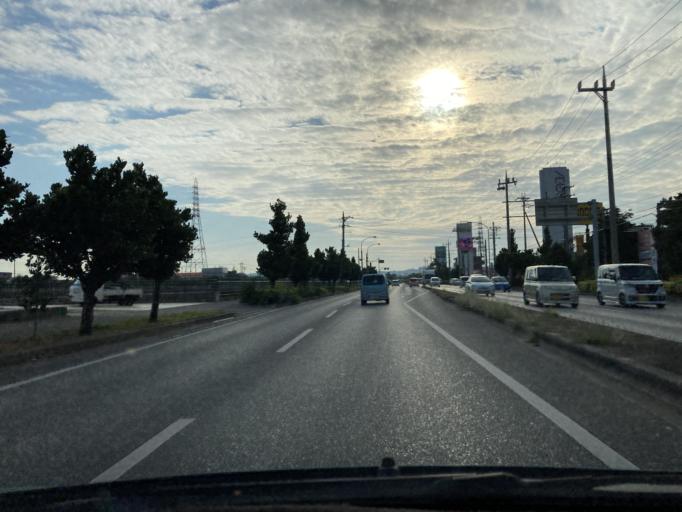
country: JP
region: Okinawa
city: Katsuren-haebaru
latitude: 26.3367
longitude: 127.8452
